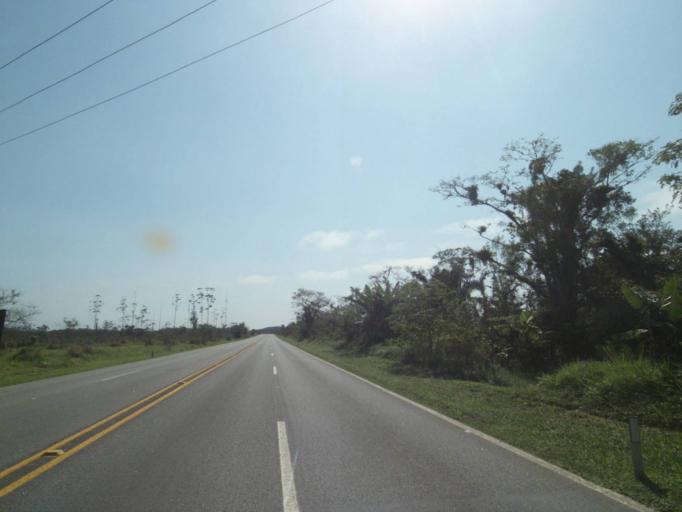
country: BR
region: Parana
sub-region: Paranagua
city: Paranagua
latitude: -25.5852
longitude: -48.6117
